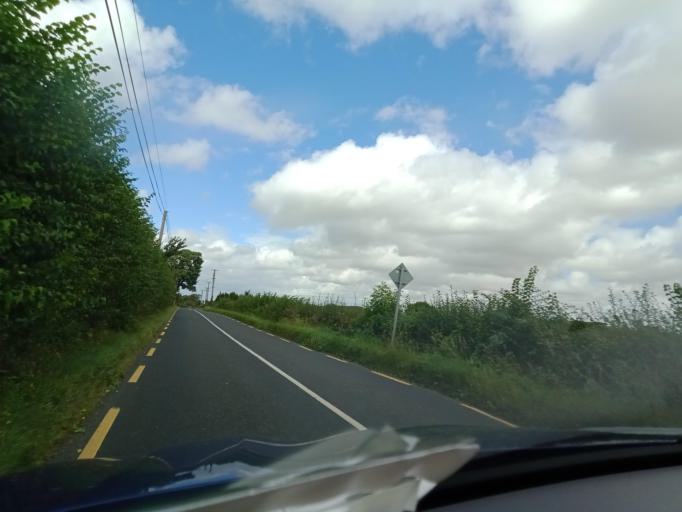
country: IE
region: Leinster
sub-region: Laois
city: Portlaoise
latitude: 52.9977
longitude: -7.2801
